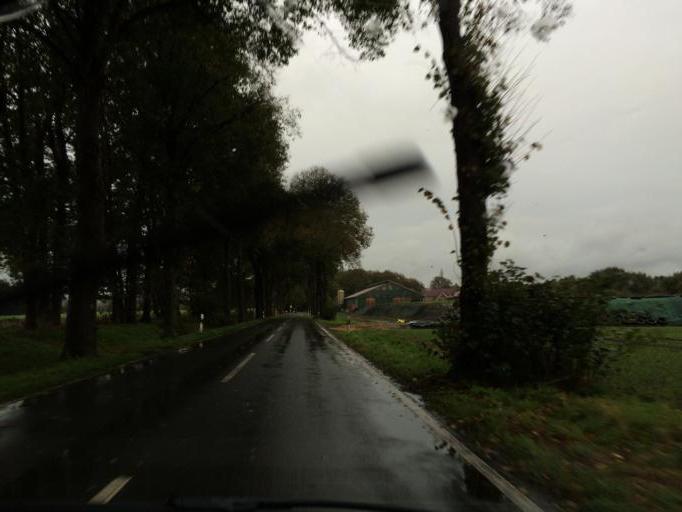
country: DE
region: North Rhine-Westphalia
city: Marl
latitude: 51.7030
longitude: 7.0761
